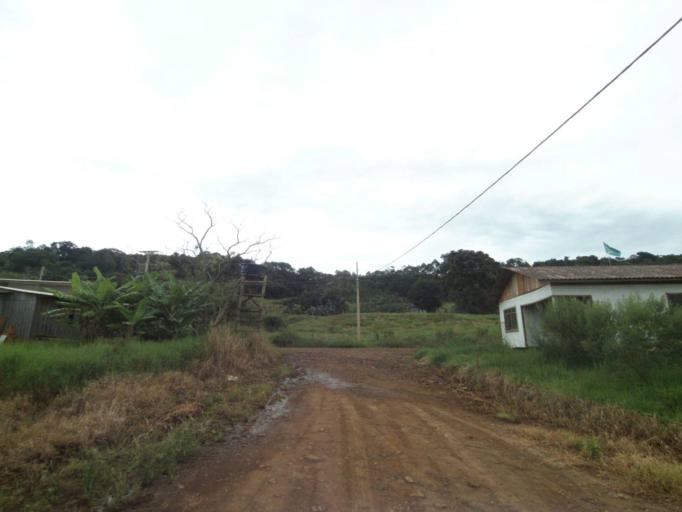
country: BR
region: Parana
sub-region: Guaraniacu
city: Guaraniacu
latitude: -25.0998
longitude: -52.8845
